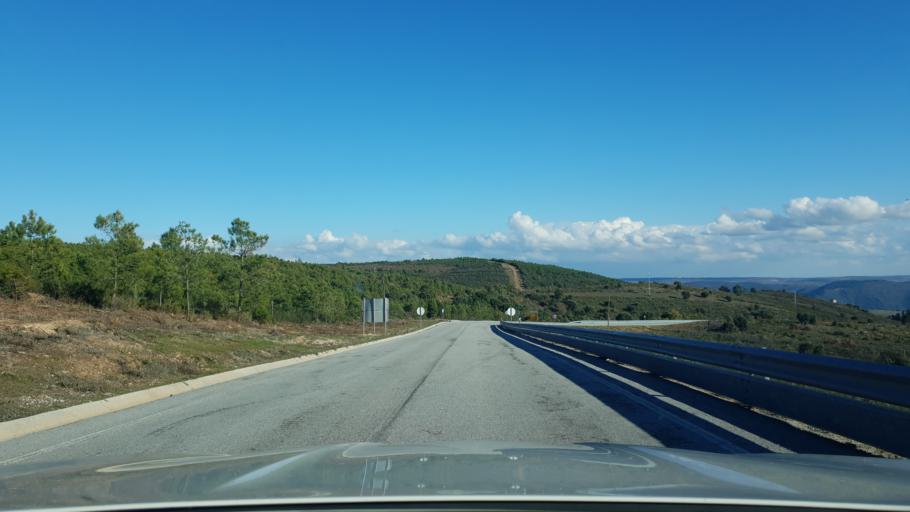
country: PT
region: Braganca
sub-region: Freixo de Espada A Cinta
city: Freixo de Espada a Cinta
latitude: 41.1282
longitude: -6.8178
